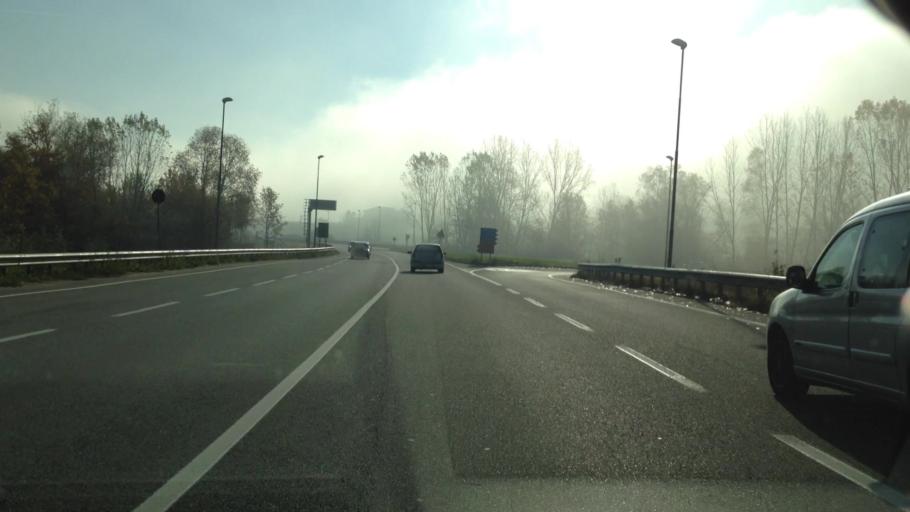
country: IT
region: Piedmont
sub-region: Provincia di Asti
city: Piano-Molini d'Isola
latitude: 44.8296
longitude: 8.2040
